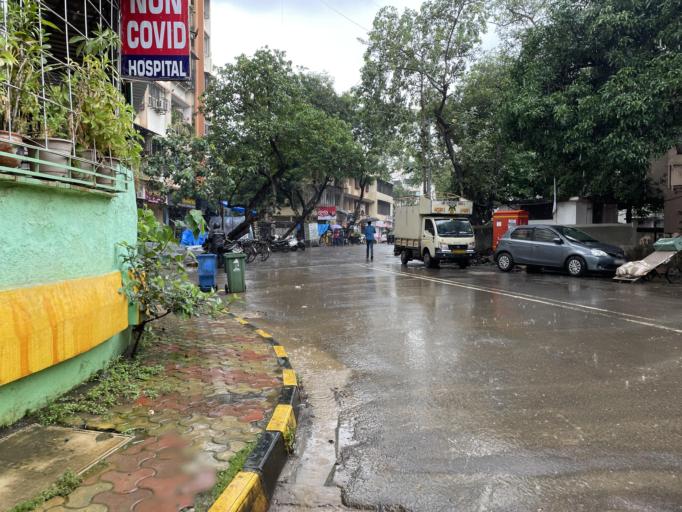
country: IN
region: Maharashtra
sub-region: Mumbai Suburban
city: Borivli
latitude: 19.2527
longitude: 72.8612
